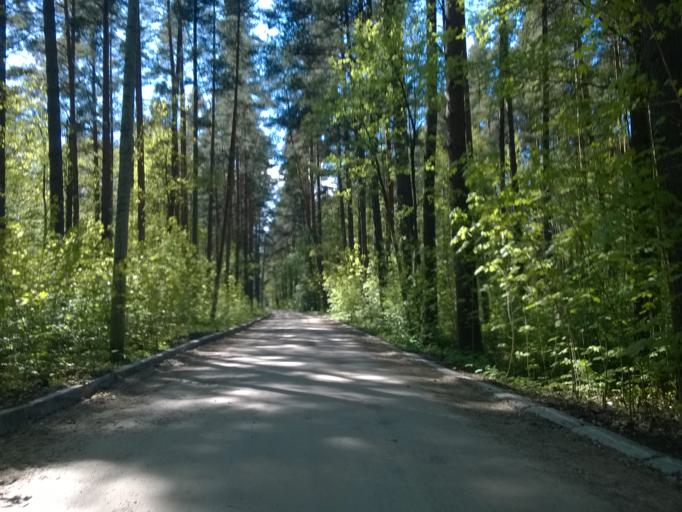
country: LV
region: Jurmala
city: Jurmala
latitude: 56.9589
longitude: 23.6523
